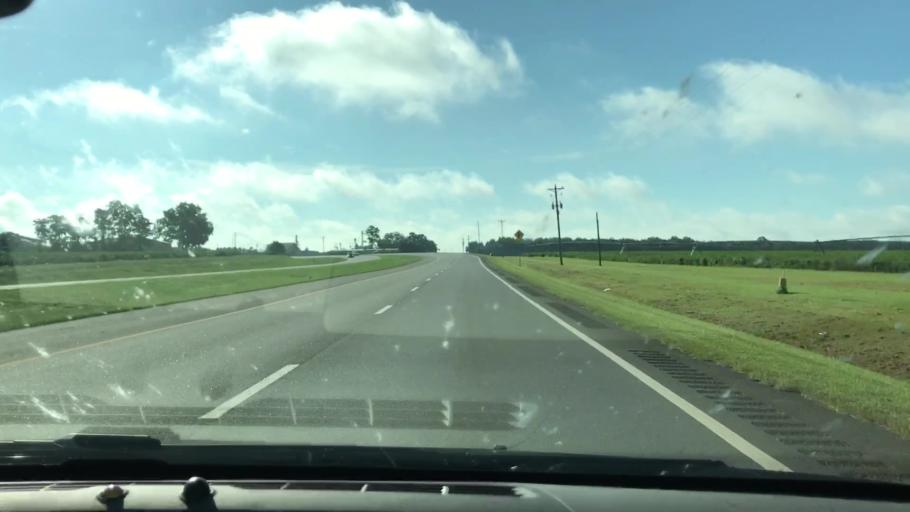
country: US
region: Georgia
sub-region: Terrell County
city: Dawson
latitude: 31.7369
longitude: -84.4052
